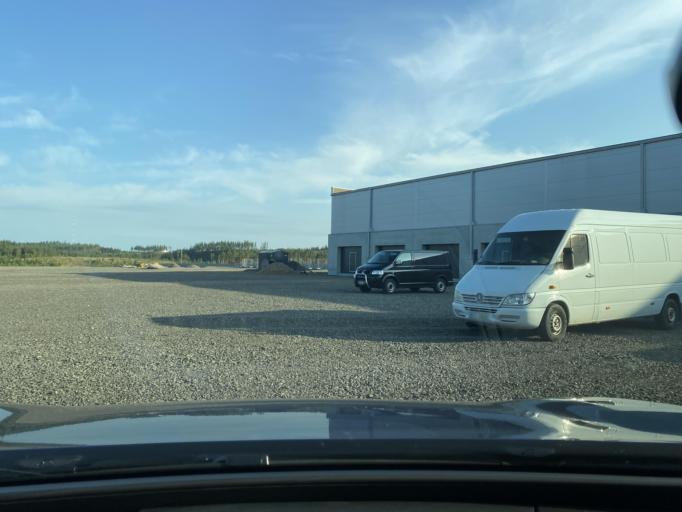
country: FI
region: Kymenlaakso
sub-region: Kouvola
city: Iitti
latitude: 60.8821
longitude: 26.4872
